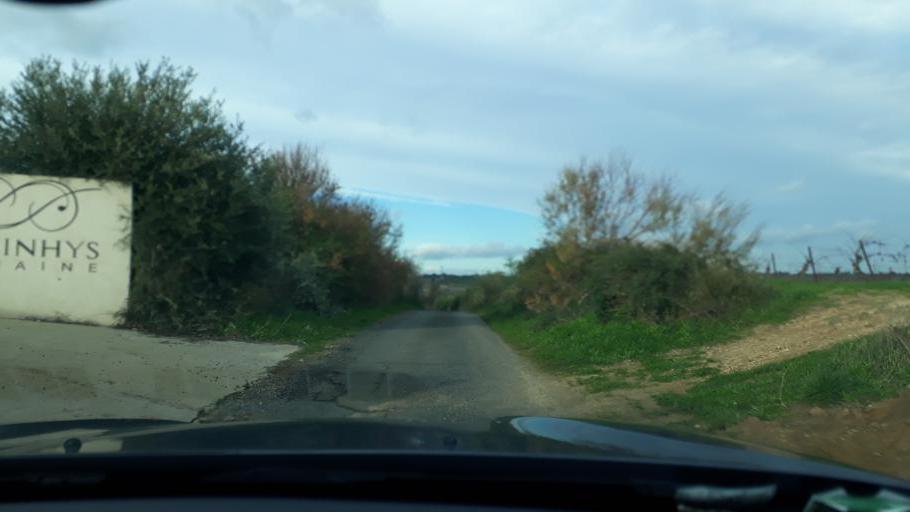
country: FR
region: Languedoc-Roussillon
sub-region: Departement de l'Herault
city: Florensac
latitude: 43.3985
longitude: 3.4594
